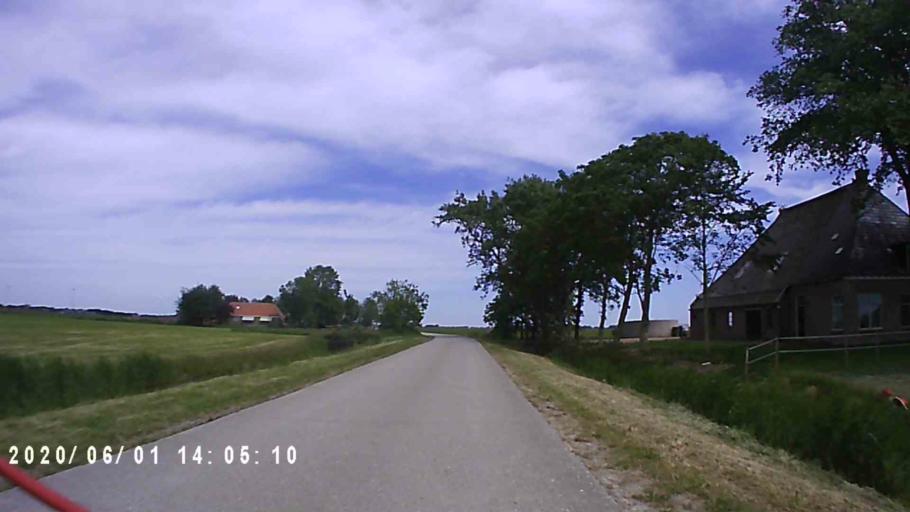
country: NL
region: Friesland
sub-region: Gemeente Littenseradiel
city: Winsum
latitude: 53.1154
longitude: 5.6356
